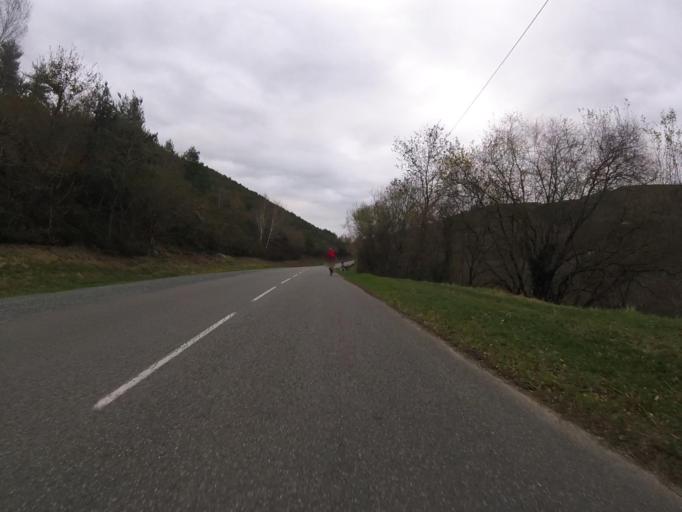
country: FR
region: Aquitaine
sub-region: Departement des Pyrenees-Atlantiques
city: Ascain
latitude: 43.3305
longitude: -1.6024
